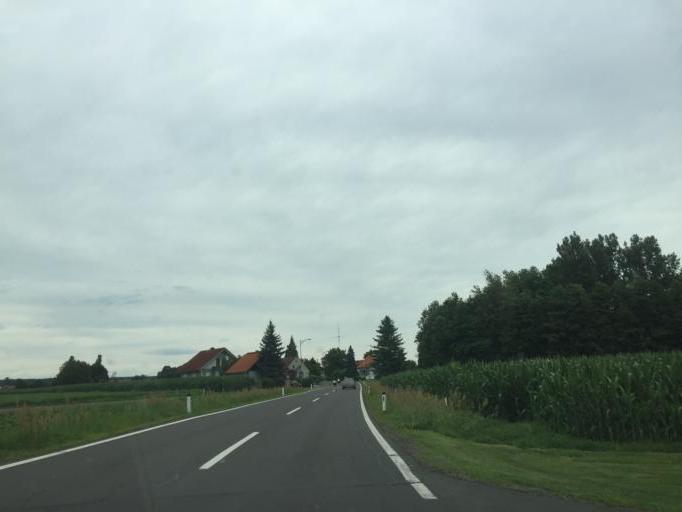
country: AT
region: Styria
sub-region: Politischer Bezirk Suedoststeiermark
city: Gosdorf
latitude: 46.7170
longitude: 15.7944
